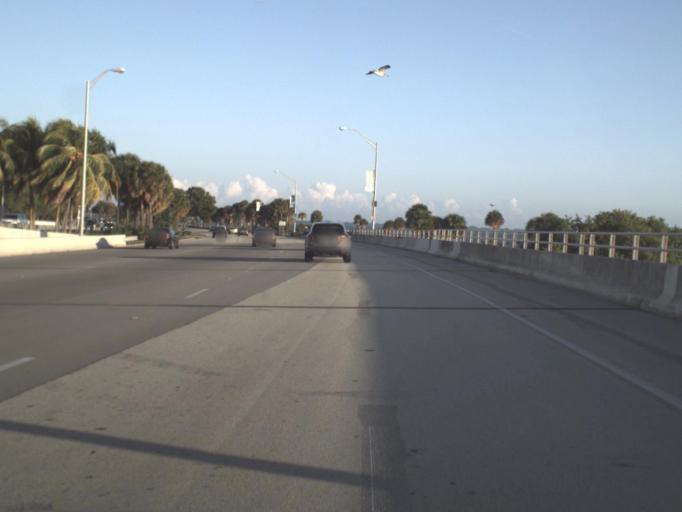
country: US
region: Florida
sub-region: Miami-Dade County
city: Miami
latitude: 25.7473
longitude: -80.2012
